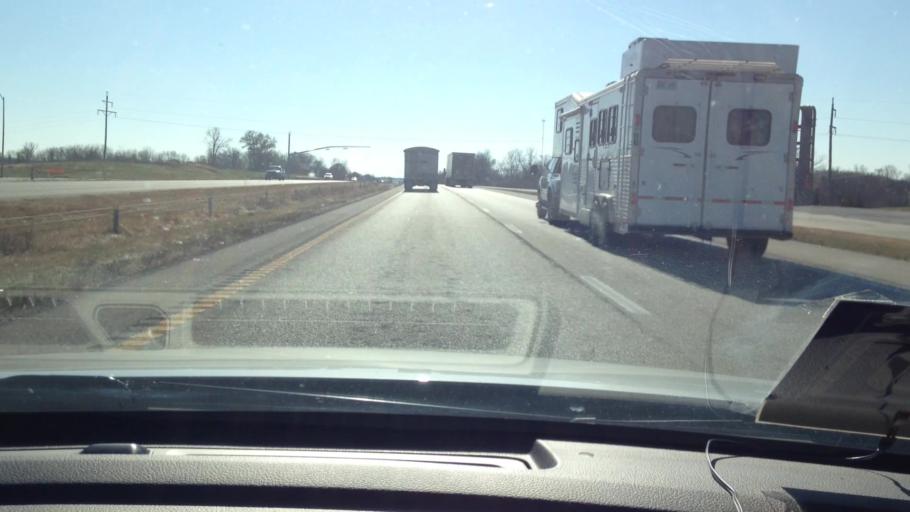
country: US
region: Missouri
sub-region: Platte County
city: Platte City
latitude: 39.4316
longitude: -94.7898
